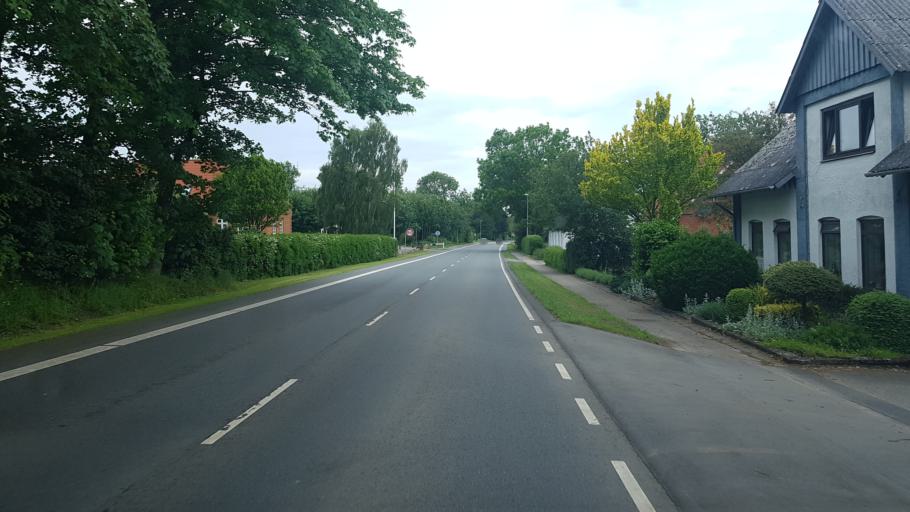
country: DK
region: South Denmark
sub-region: Vejen Kommune
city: Brorup
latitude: 55.4300
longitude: 9.0135
